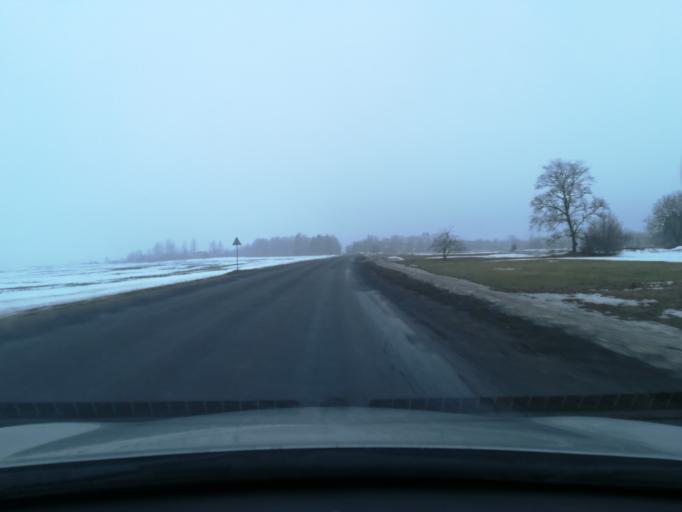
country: EE
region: Harju
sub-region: Raasiku vald
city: Arukula
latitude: 59.3446
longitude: 25.1080
